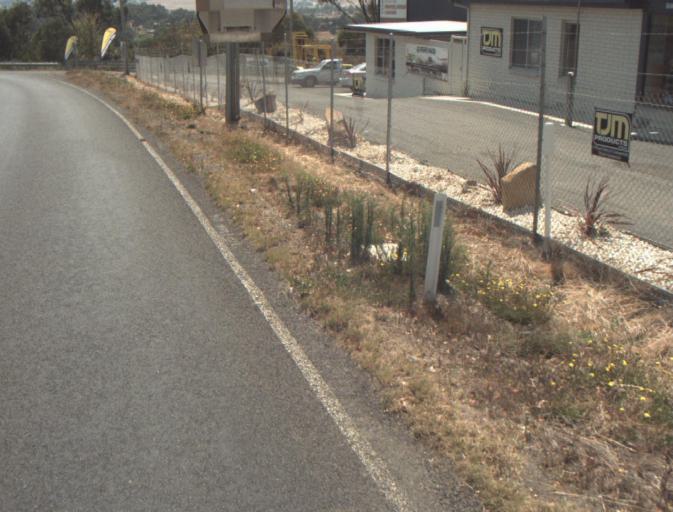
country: AU
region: Tasmania
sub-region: Launceston
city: Summerhill
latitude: -41.4975
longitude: 147.1719
